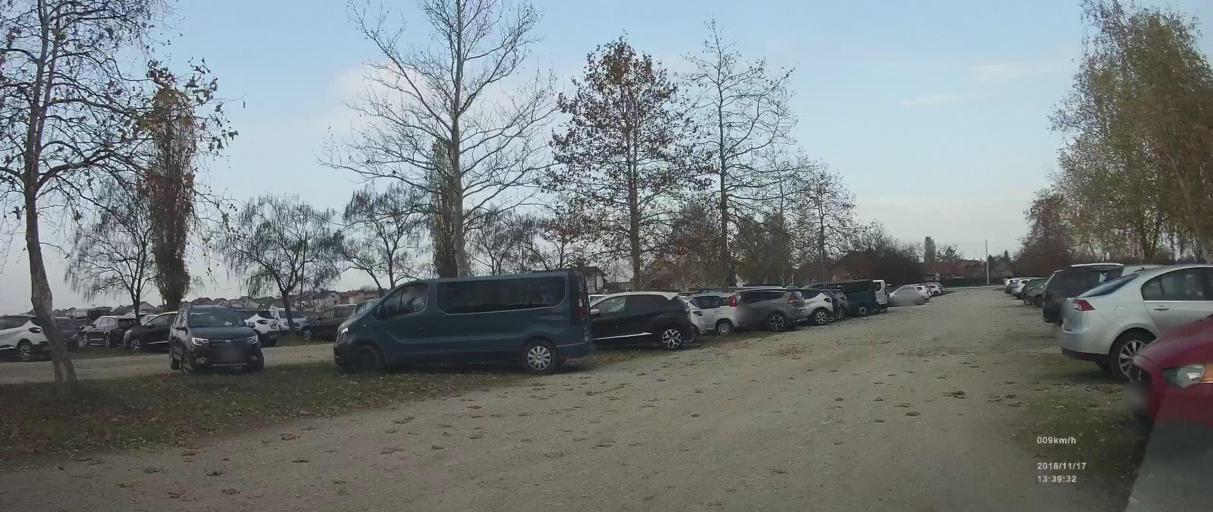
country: HR
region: Zagrebacka
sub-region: Grad Velika Gorica
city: Velika Gorica
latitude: 45.7235
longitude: 16.0704
